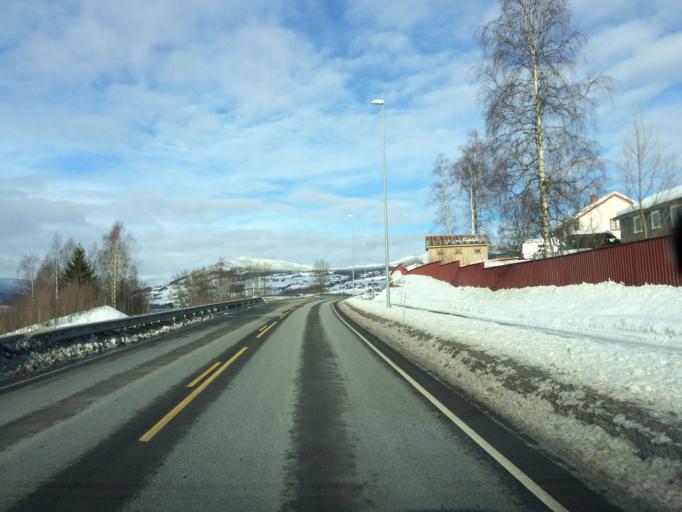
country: NO
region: Oppland
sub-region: Gausdal
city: Segalstad bru
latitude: 61.1959
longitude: 10.3107
